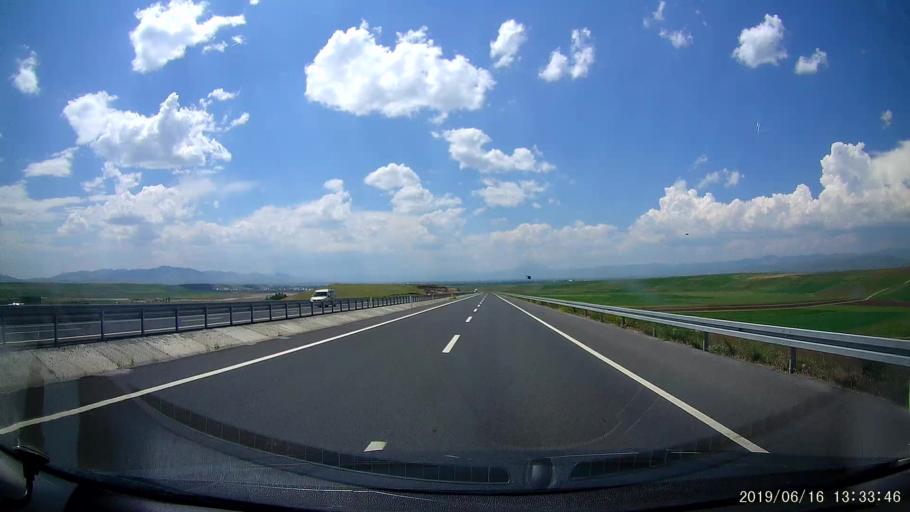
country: TR
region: Agri
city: Agri
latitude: 39.7085
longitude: 43.1454
